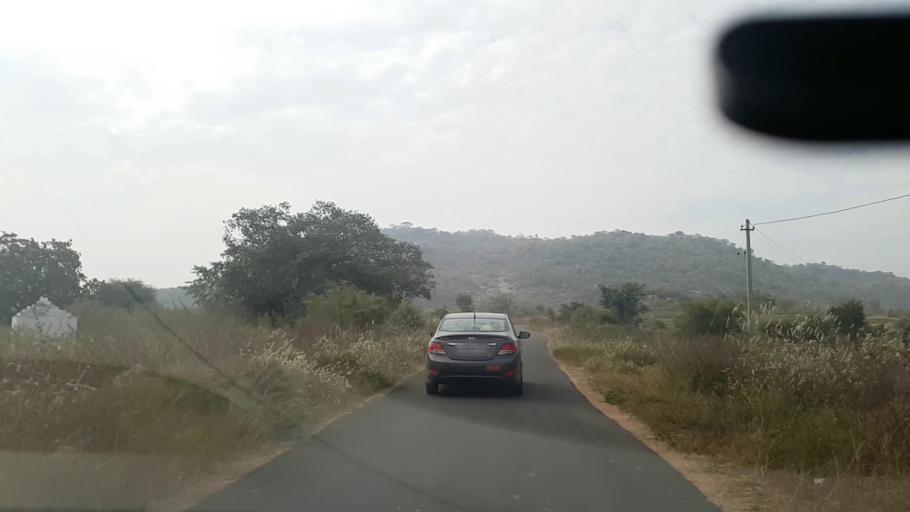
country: IN
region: Telangana
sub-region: Rangareddi
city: Ghatkesar
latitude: 17.1746
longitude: 78.8197
